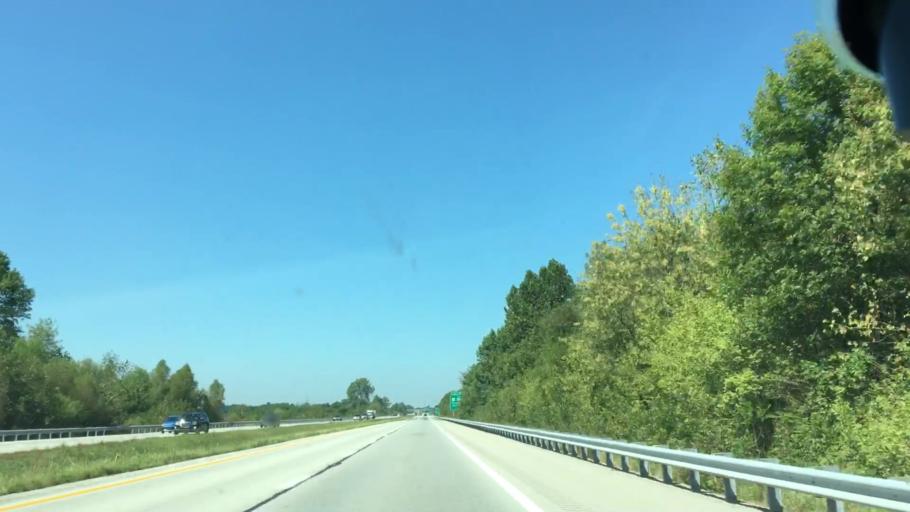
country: US
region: Kentucky
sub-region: Henderson County
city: Henderson
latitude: 37.7810
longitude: -87.5449
